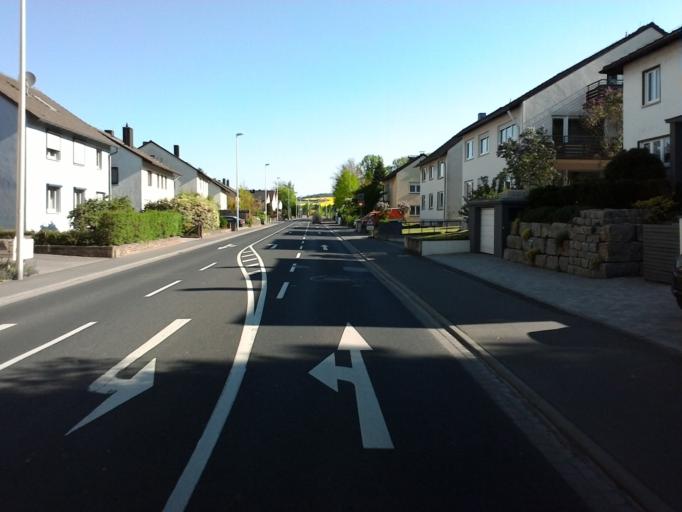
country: DE
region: Bavaria
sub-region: Regierungsbezirk Unterfranken
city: Marktheidenfeld
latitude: 49.8422
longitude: 9.6125
